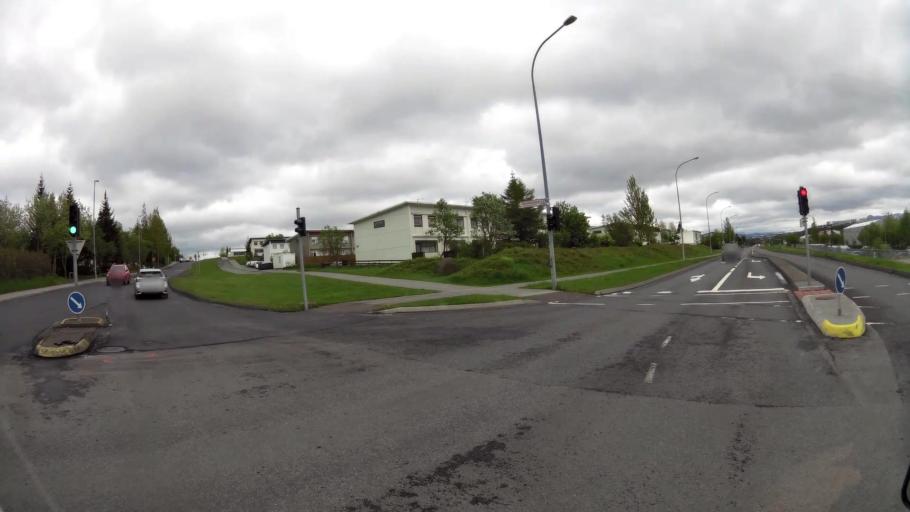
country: IS
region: Capital Region
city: Reykjavik
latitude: 64.1218
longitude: -21.8696
